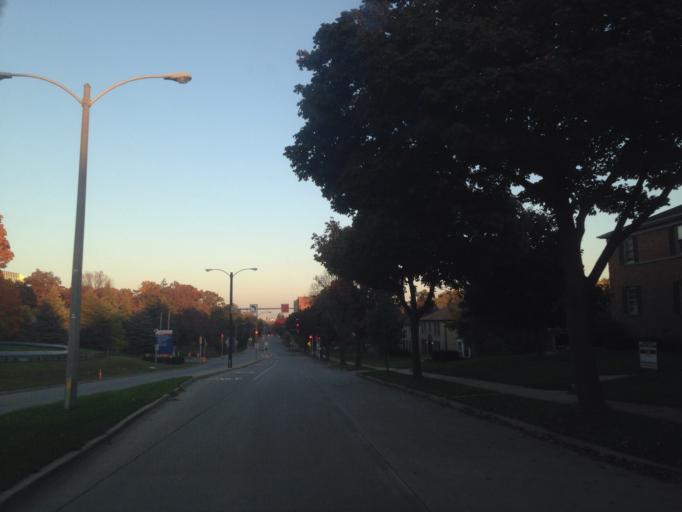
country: US
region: Wisconsin
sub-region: Milwaukee County
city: Wauwatosa
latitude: 43.0383
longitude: -88.0288
